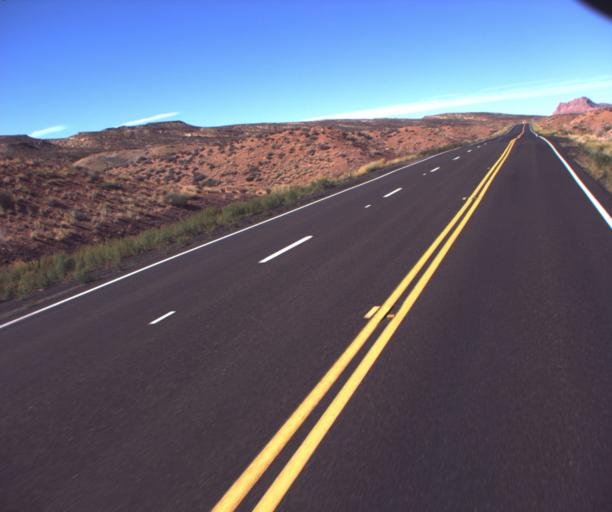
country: US
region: Arizona
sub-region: Coconino County
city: Tuba City
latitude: 36.2331
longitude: -111.4063
